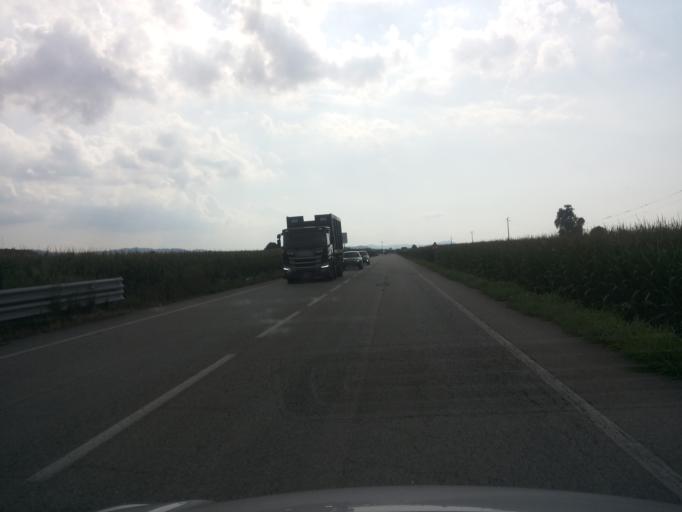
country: IT
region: Piedmont
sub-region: Provincia di Alessandria
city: Villanova Monferrato
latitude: 45.1613
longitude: 8.4742
